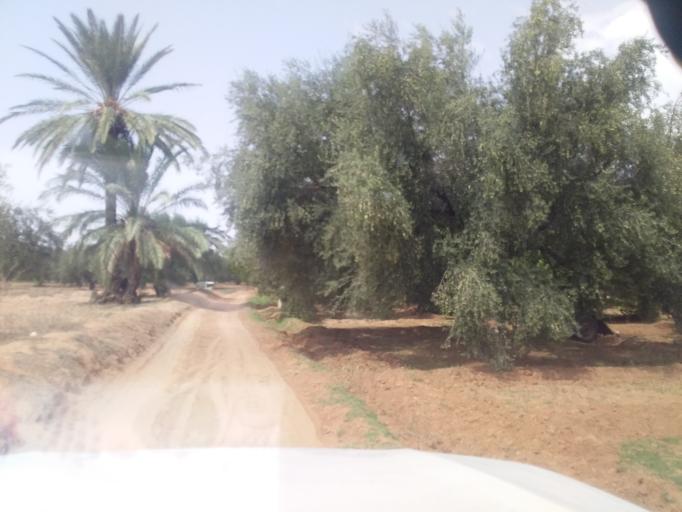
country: TN
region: Madanin
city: Medenine
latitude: 33.5982
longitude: 10.3252
